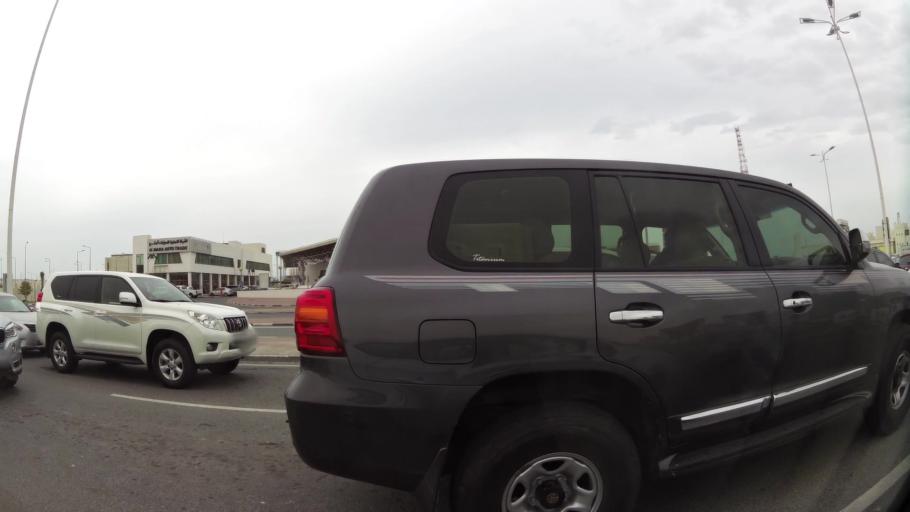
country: QA
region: Baladiyat ad Dawhah
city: Doha
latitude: 25.3112
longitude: 51.4962
